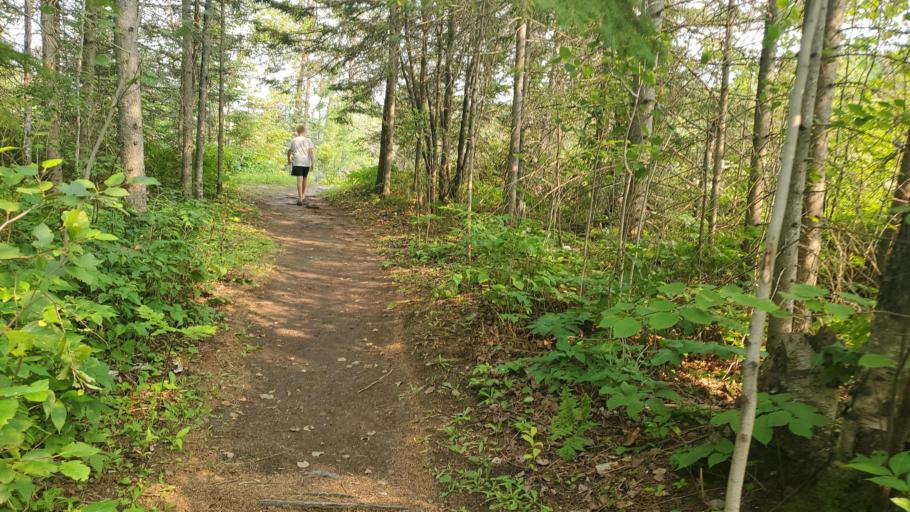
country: CA
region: Ontario
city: Englehart
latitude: 47.7965
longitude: -79.8863
